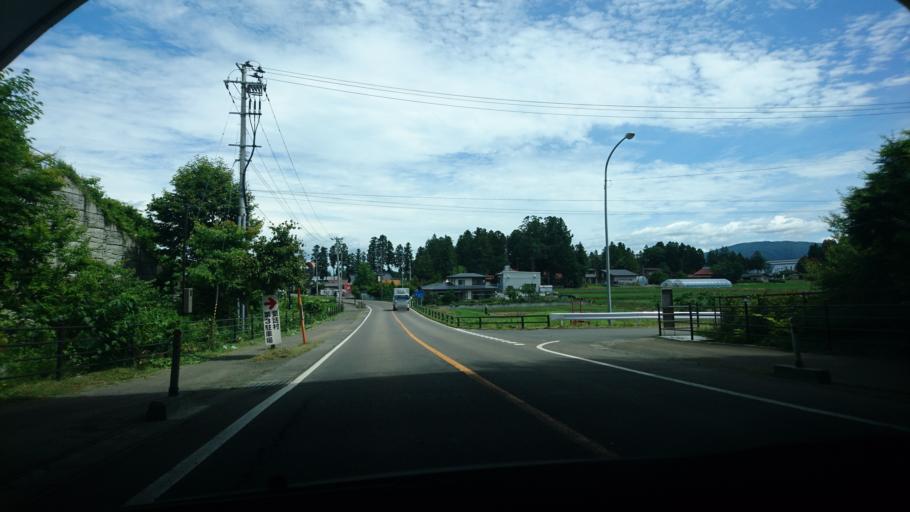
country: JP
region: Iwate
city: Hanamaki
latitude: 39.4020
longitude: 141.1679
